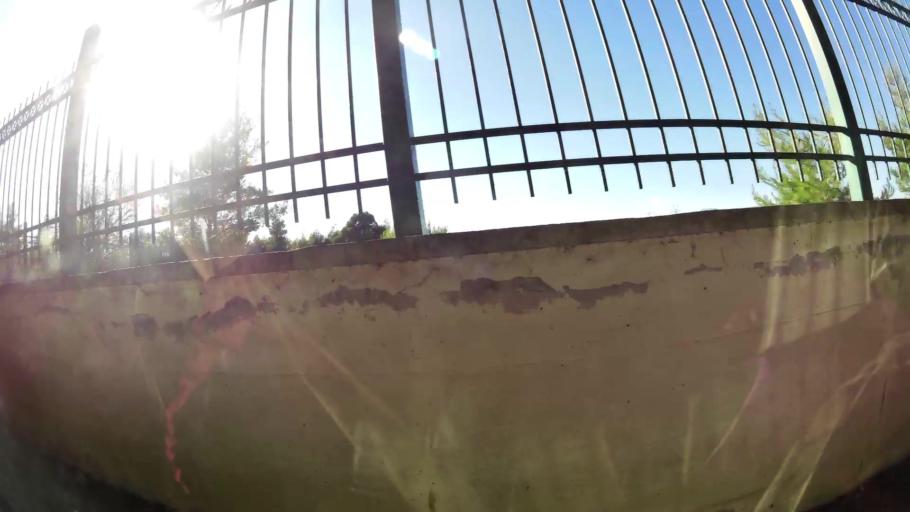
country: GR
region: Attica
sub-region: Nomarchia Anatolikis Attikis
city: Anoixi
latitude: 38.1226
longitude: 23.8531
